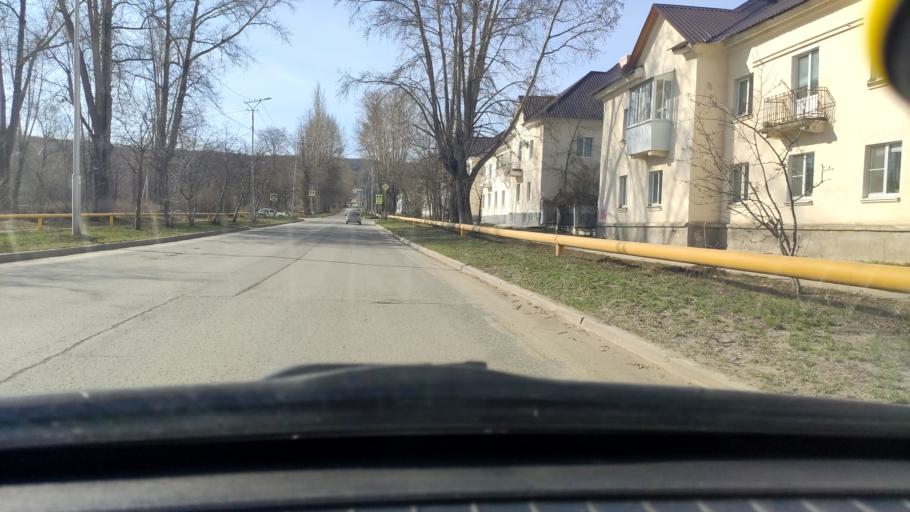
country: RU
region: Samara
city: Zhigulevsk
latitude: 53.4001
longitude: 49.4976
